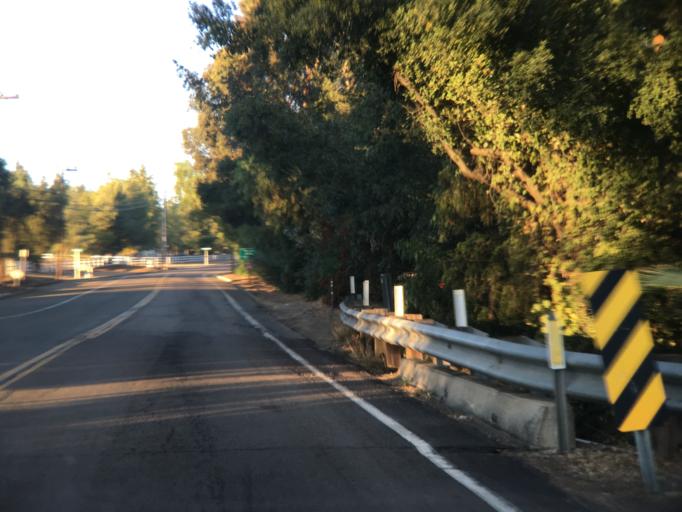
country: US
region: California
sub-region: San Diego County
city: Alpine
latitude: 32.8086
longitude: -116.7806
